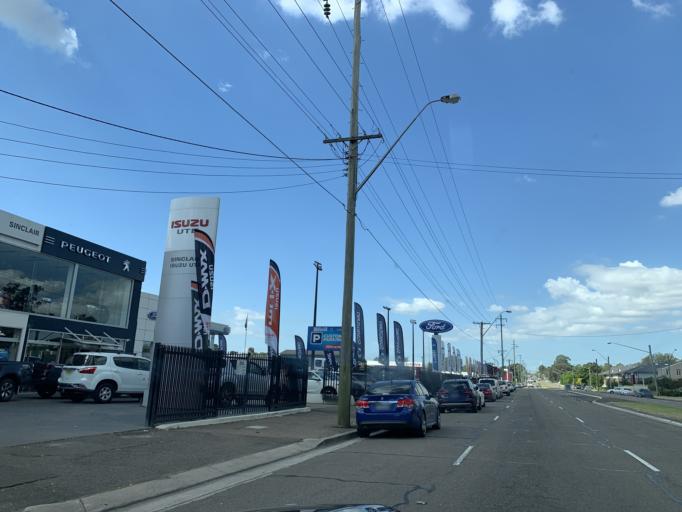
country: AU
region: New South Wales
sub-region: Penrith Municipality
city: Cambridge Park
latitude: -33.7601
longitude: 150.7267
